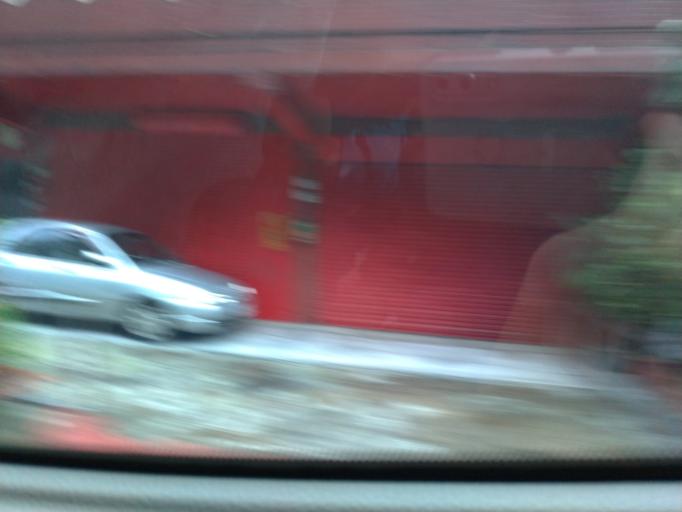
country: TW
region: Taipei
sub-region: Taipei
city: Banqiao
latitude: 24.9279
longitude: 121.4245
